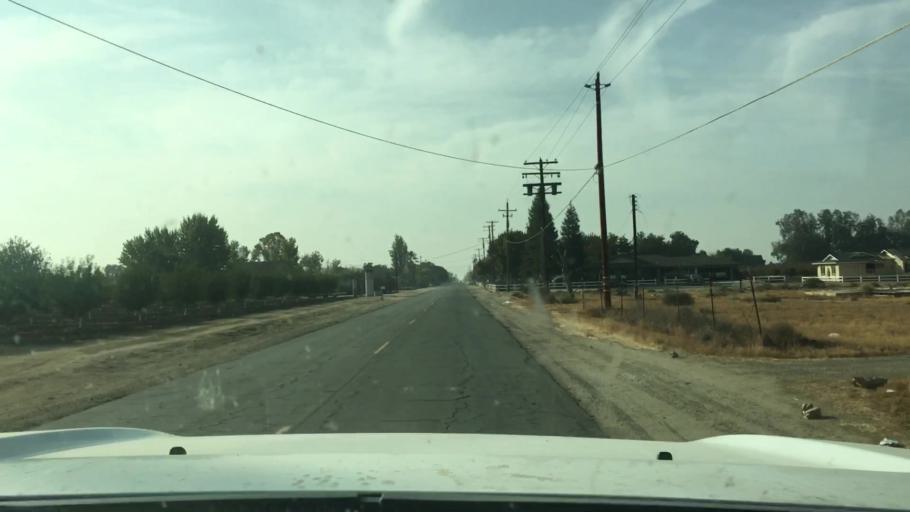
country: US
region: California
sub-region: Kern County
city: Shafter
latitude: 35.4854
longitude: -119.2862
